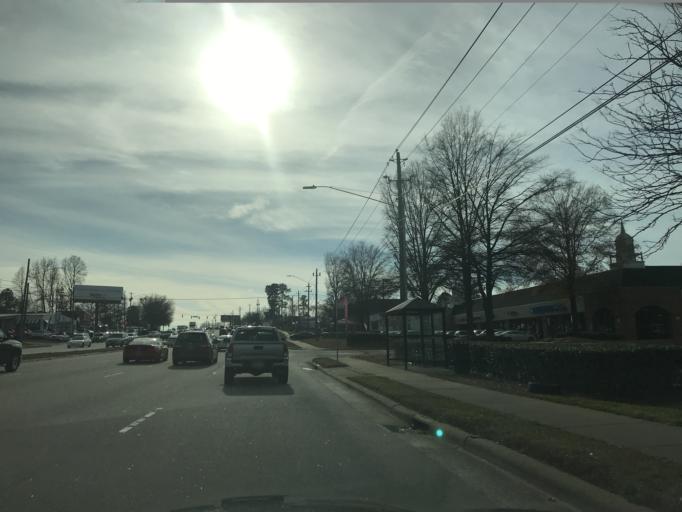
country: US
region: North Carolina
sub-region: Wake County
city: Raleigh
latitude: 35.8344
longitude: -78.5832
